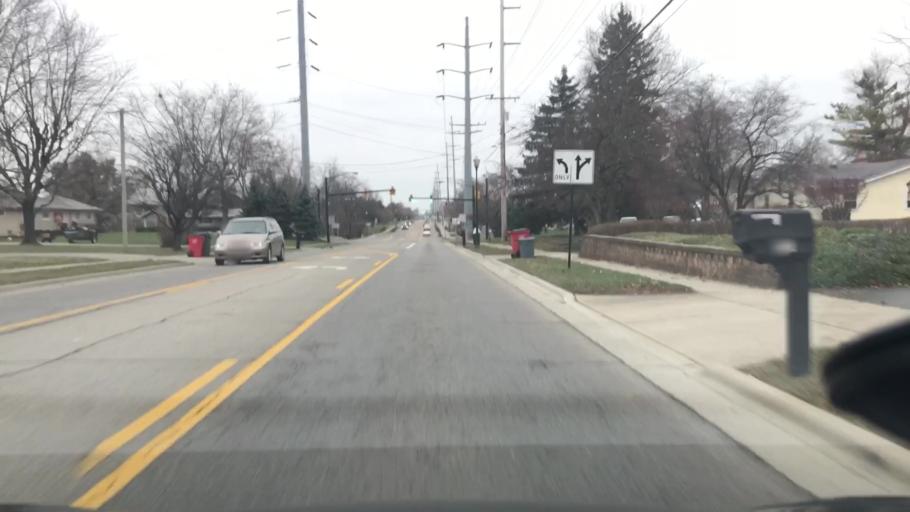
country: US
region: Ohio
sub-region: Franklin County
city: Grove City
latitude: 39.8741
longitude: -83.0702
